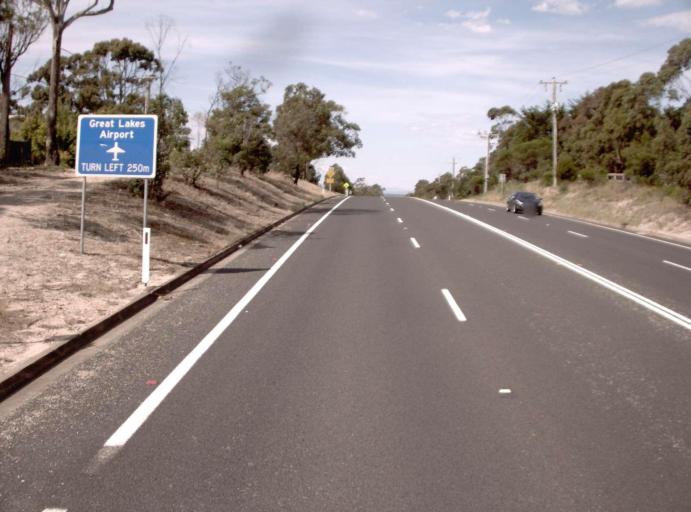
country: AU
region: Victoria
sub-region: East Gippsland
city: Lakes Entrance
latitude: -37.8634
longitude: 148.0241
